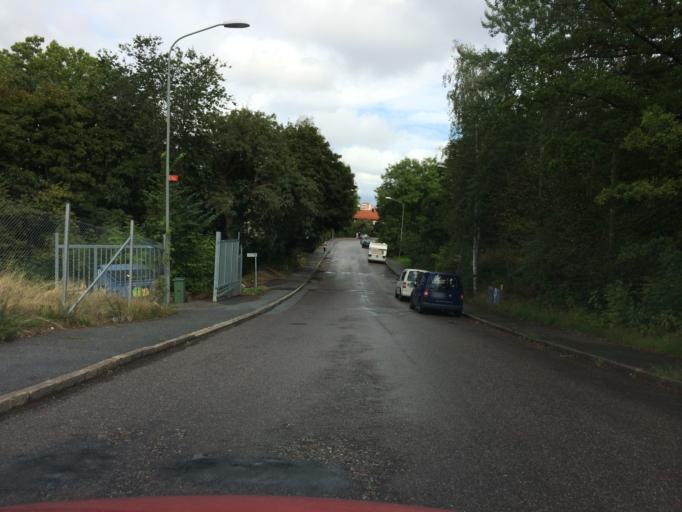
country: SE
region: Stockholm
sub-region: Stockholms Kommun
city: Bromma
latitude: 59.3067
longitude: 17.9716
